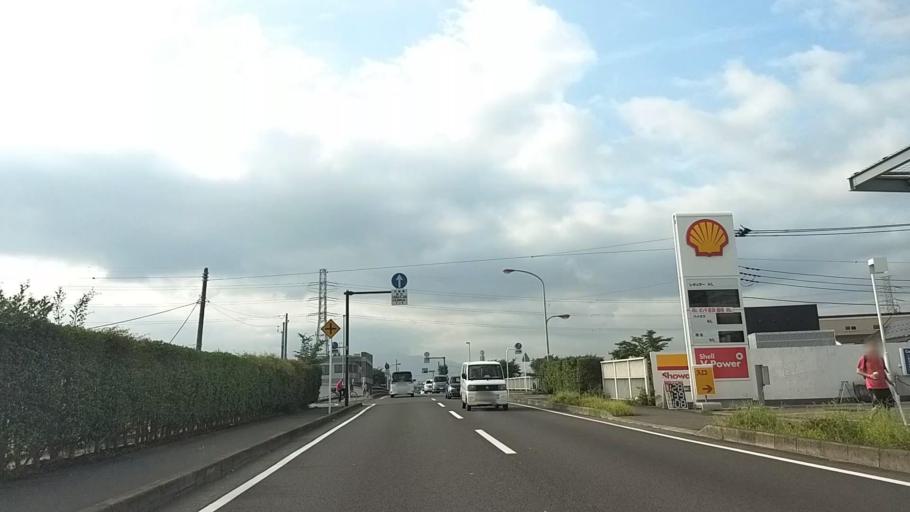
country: JP
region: Kanagawa
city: Hiratsuka
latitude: 35.3515
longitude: 139.3304
